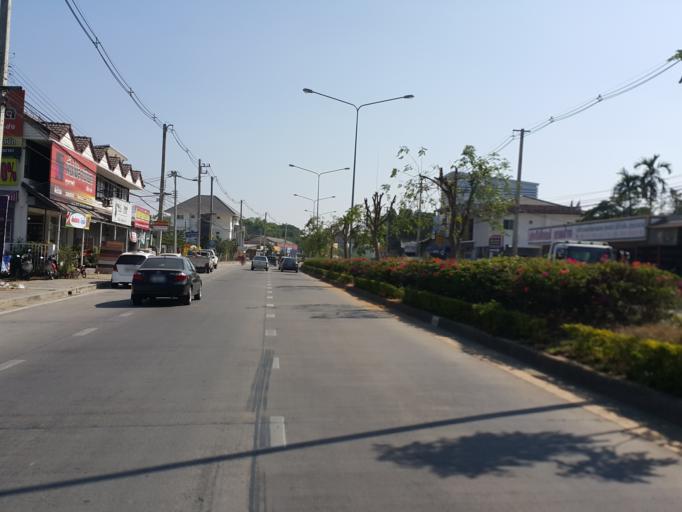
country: TH
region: Chiang Mai
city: San Sai
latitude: 18.8066
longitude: 99.0287
